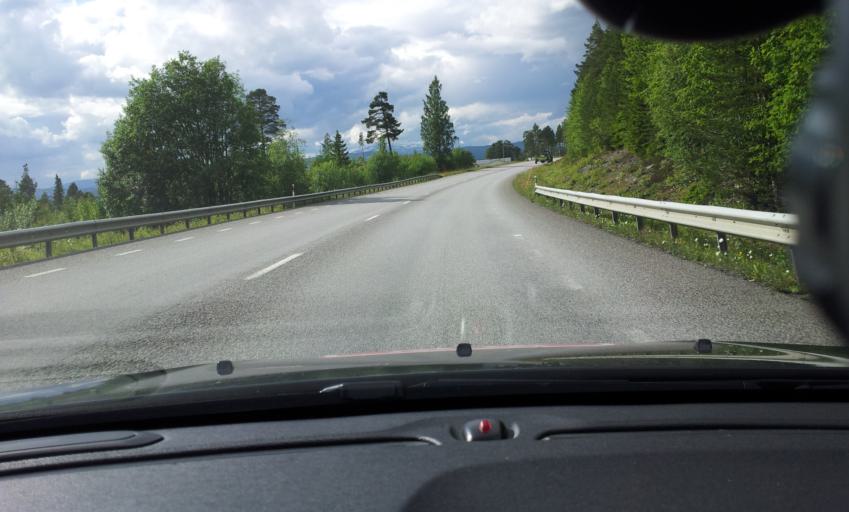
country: SE
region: Jaemtland
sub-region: Are Kommun
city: Jarpen
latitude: 63.3227
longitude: 13.5447
